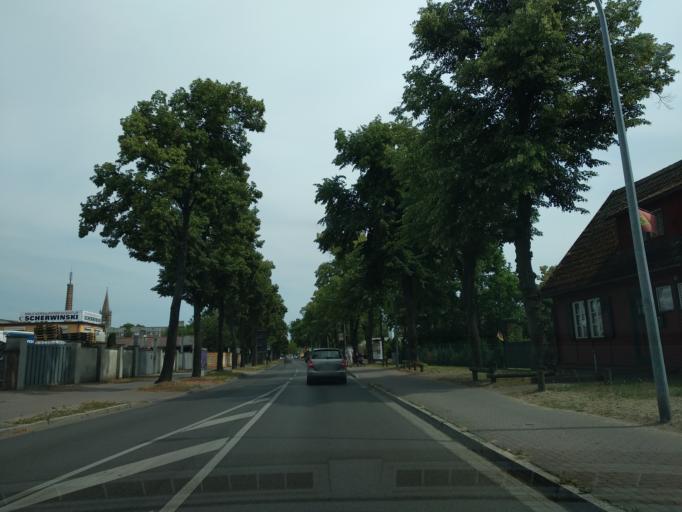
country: DE
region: Brandenburg
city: Oranienburg
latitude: 52.7509
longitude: 13.2273
